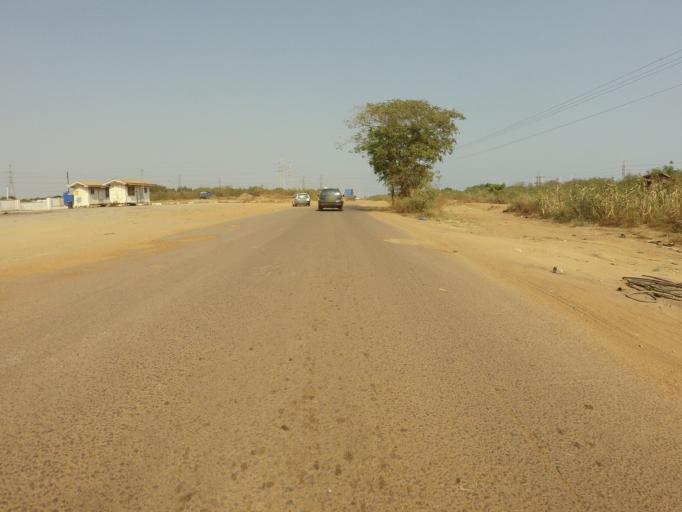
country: GH
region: Greater Accra
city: Tema
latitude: 5.6700
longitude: 0.0175
